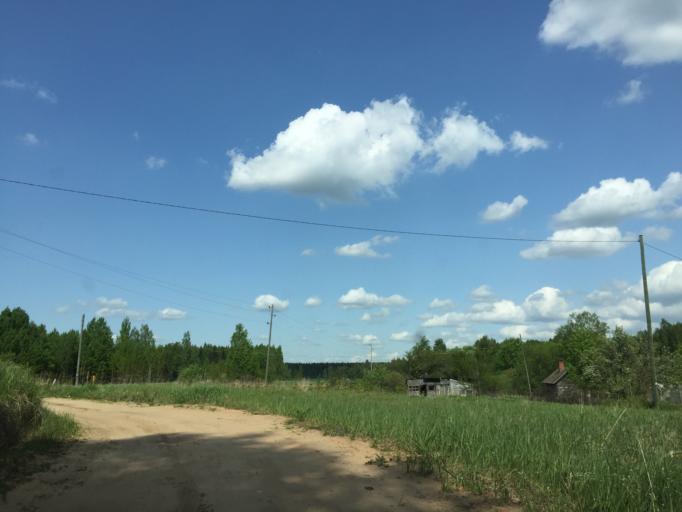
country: LV
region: Baldone
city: Baldone
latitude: 56.7890
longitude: 24.4157
